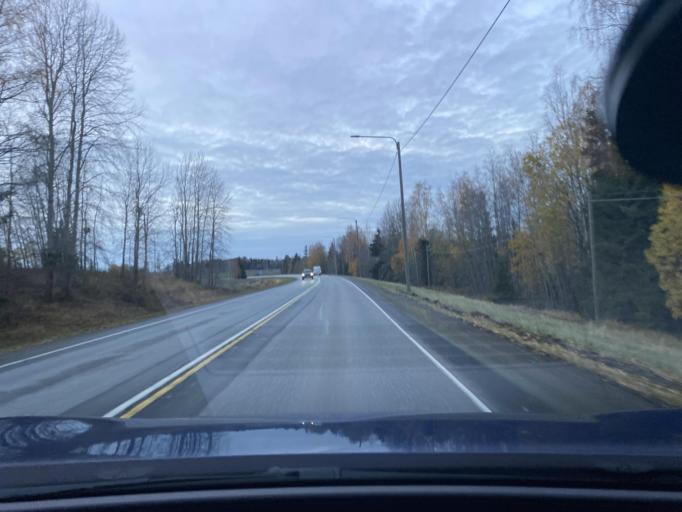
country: FI
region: Uusimaa
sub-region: Helsinki
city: Lohja
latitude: 60.3664
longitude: 24.1619
